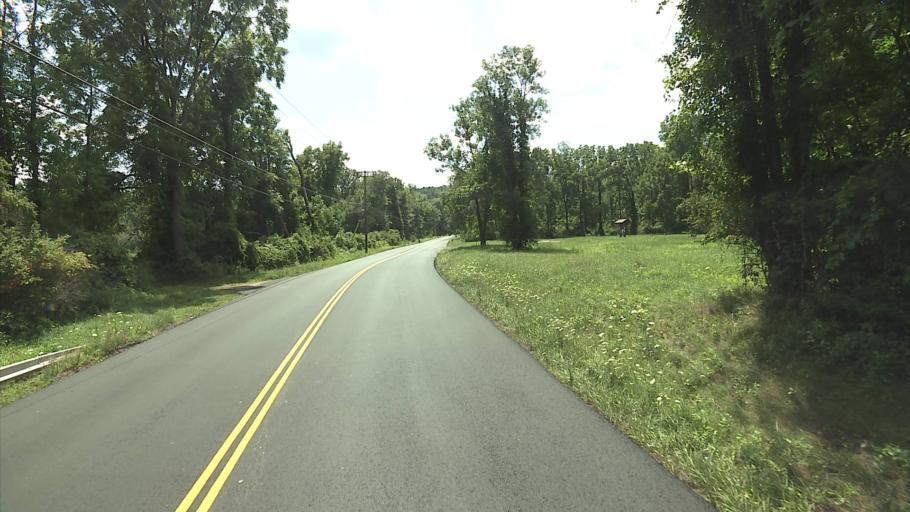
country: US
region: Connecticut
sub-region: Litchfield County
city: Canaan
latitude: 41.9697
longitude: -73.3583
